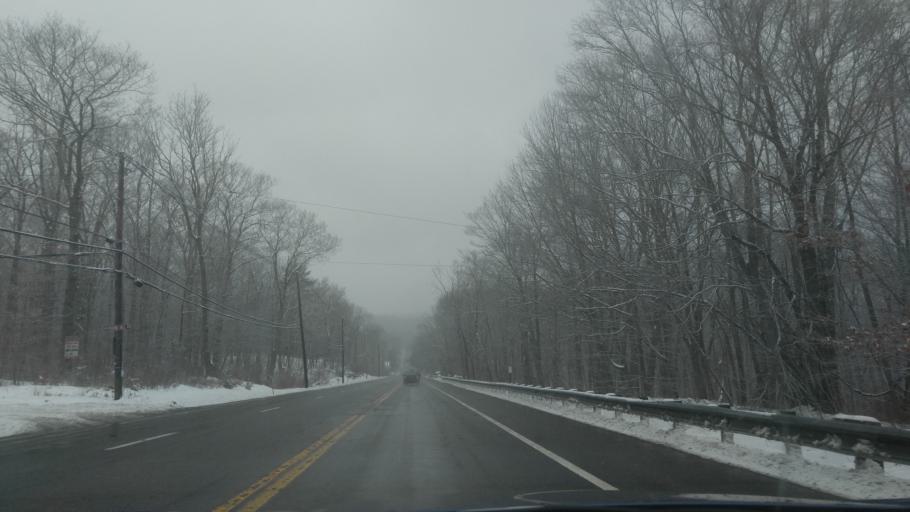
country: US
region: Rhode Island
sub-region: Providence County
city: Foster
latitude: 41.8229
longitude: -71.6929
